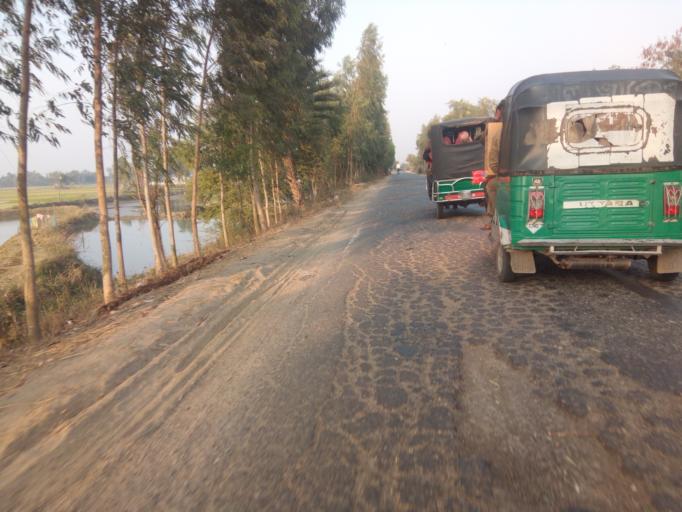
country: BD
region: Rajshahi
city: Par Naogaon
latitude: 24.5060
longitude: 89.1520
